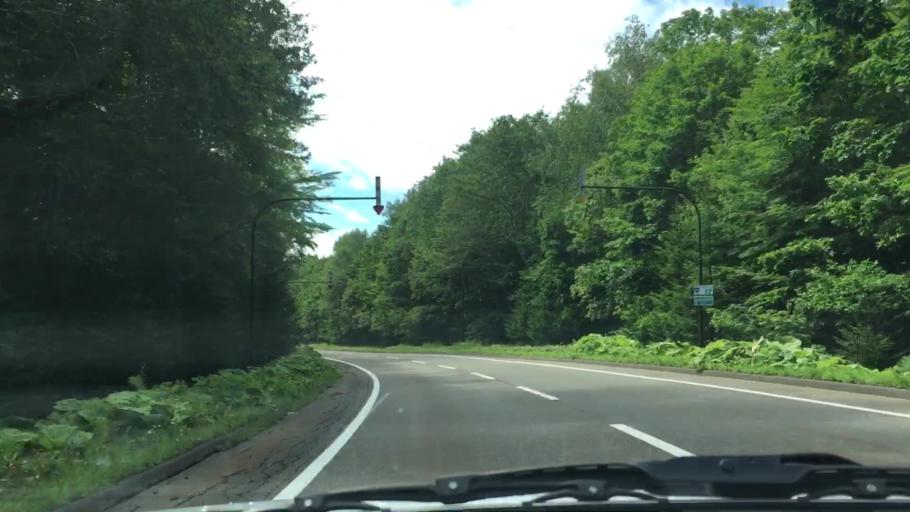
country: JP
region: Hokkaido
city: Kitami
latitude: 43.3988
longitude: 143.9264
